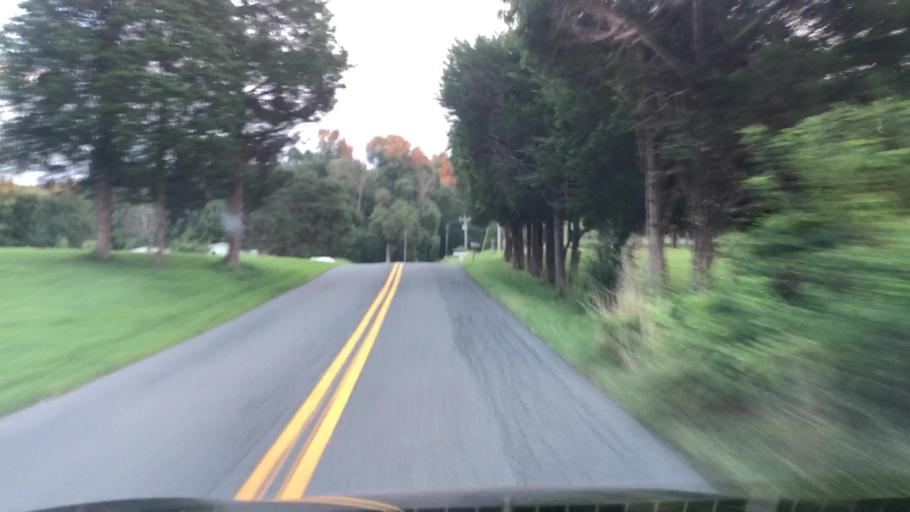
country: US
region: Virginia
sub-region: Stafford County
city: Stafford
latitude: 38.4752
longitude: -77.5792
